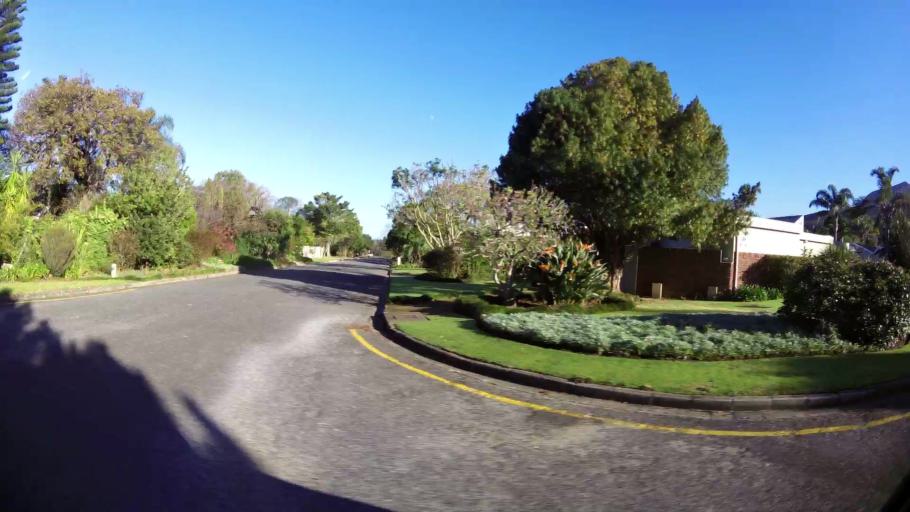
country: ZA
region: Western Cape
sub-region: Eden District Municipality
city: George
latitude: -33.9451
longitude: 22.4541
